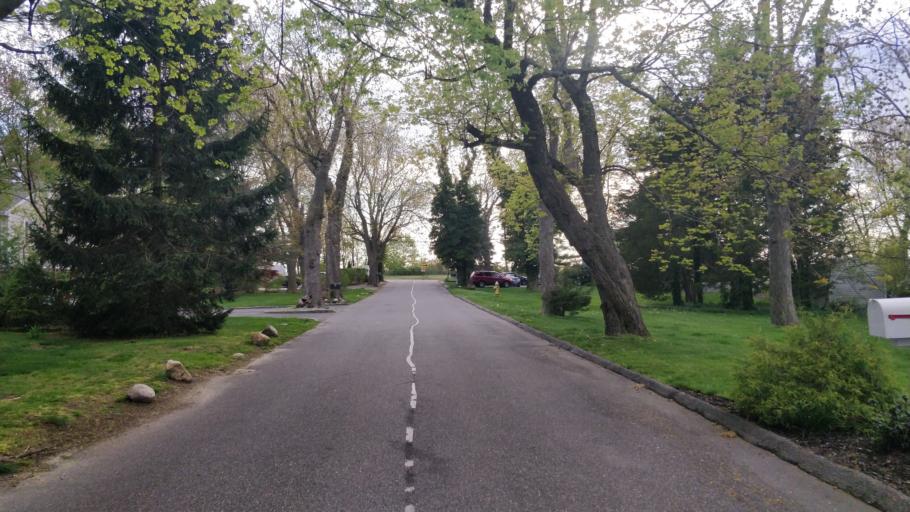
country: US
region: New York
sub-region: Suffolk County
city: Northport
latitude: 40.9103
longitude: -73.3435
